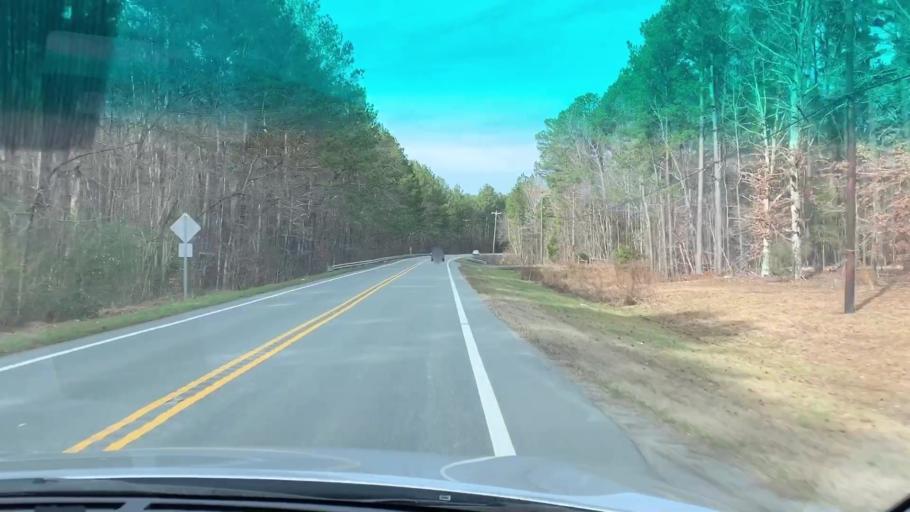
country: US
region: North Carolina
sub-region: Wake County
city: Green Level
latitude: 35.8507
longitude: -78.9356
